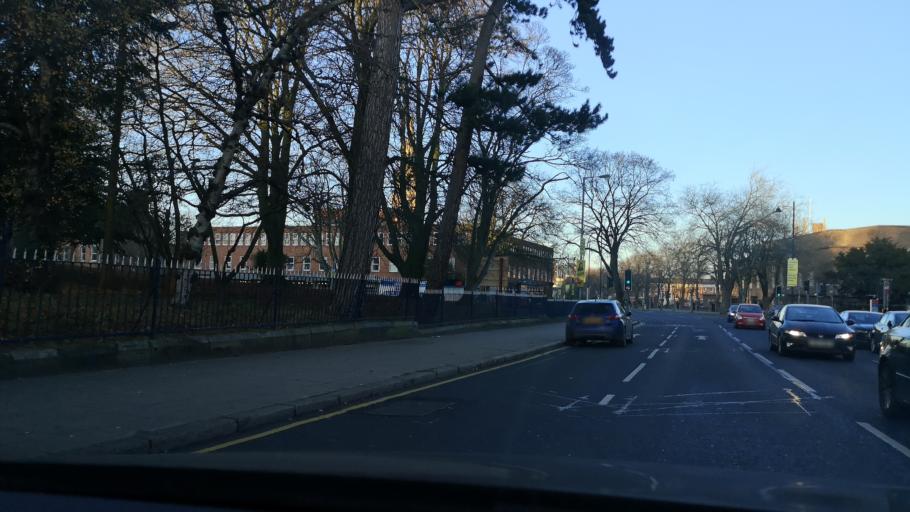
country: GB
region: Northern Ireland
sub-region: City of Belfast
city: Belfast
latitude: 54.5826
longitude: -5.9373
